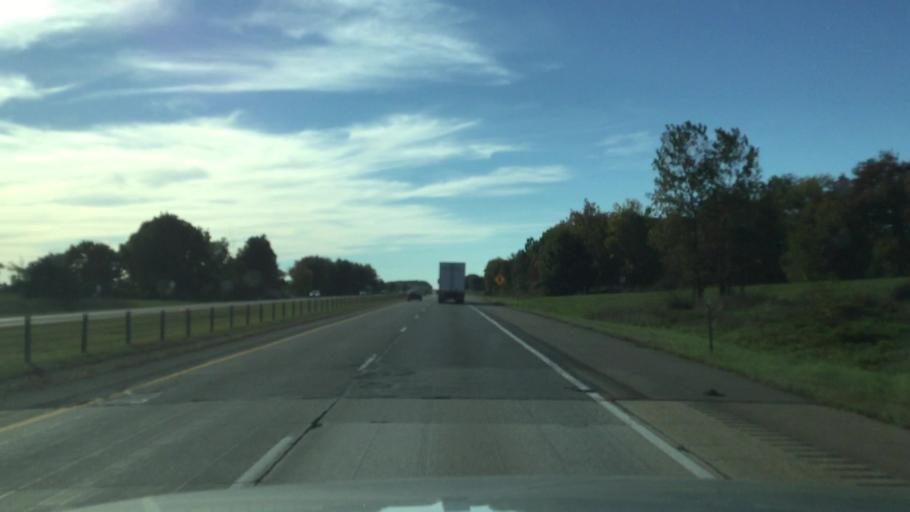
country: US
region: Michigan
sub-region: Calhoun County
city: Albion
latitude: 42.2839
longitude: -84.8013
